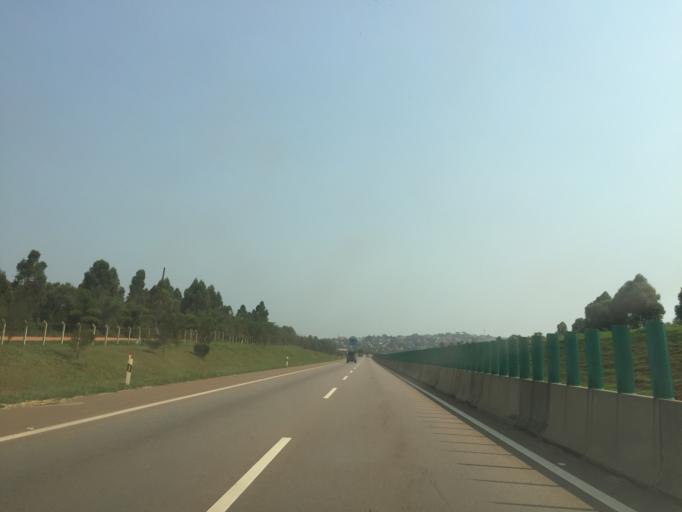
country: UG
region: Central Region
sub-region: Wakiso District
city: Kajansi
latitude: 0.2237
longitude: 32.5281
